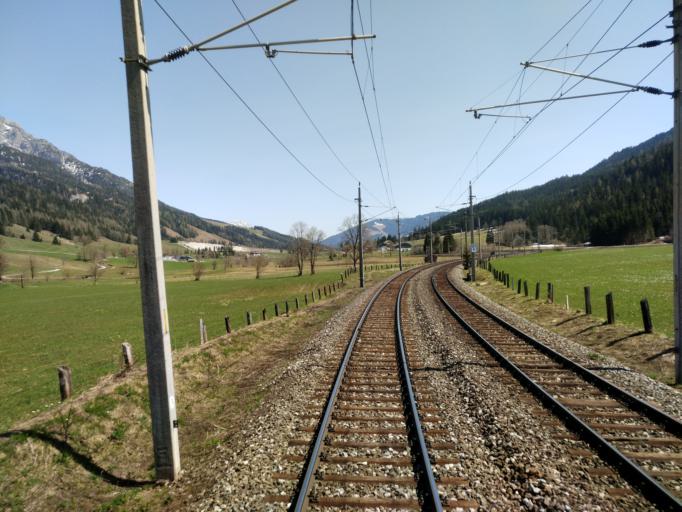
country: AT
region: Tyrol
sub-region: Politischer Bezirk Kitzbuhel
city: Hochfilzen
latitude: 47.4560
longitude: 12.6548
